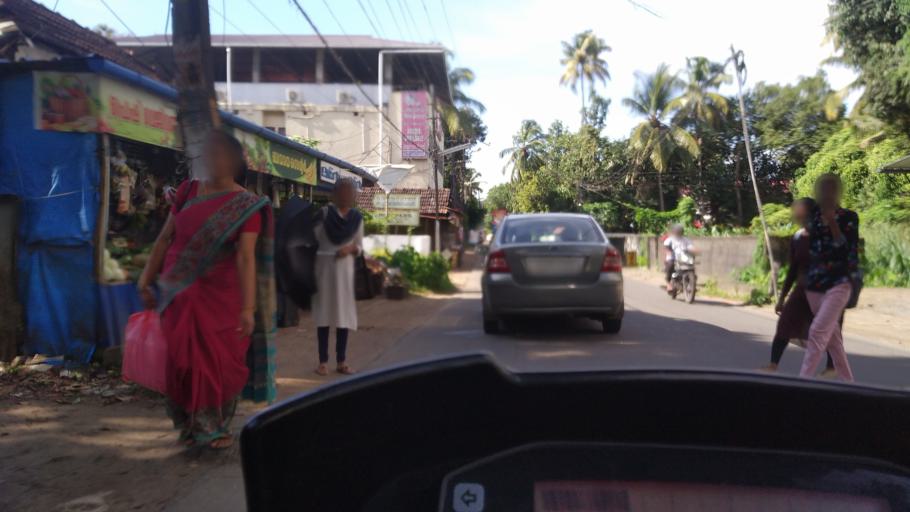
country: IN
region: Kerala
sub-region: Ernakulam
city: Elur
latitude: 10.0494
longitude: 76.2168
